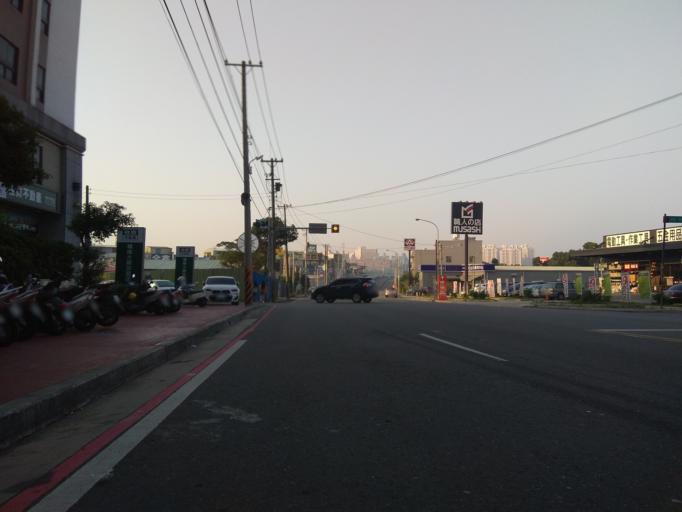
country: TW
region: Taiwan
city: Daxi
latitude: 24.9097
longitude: 121.1751
